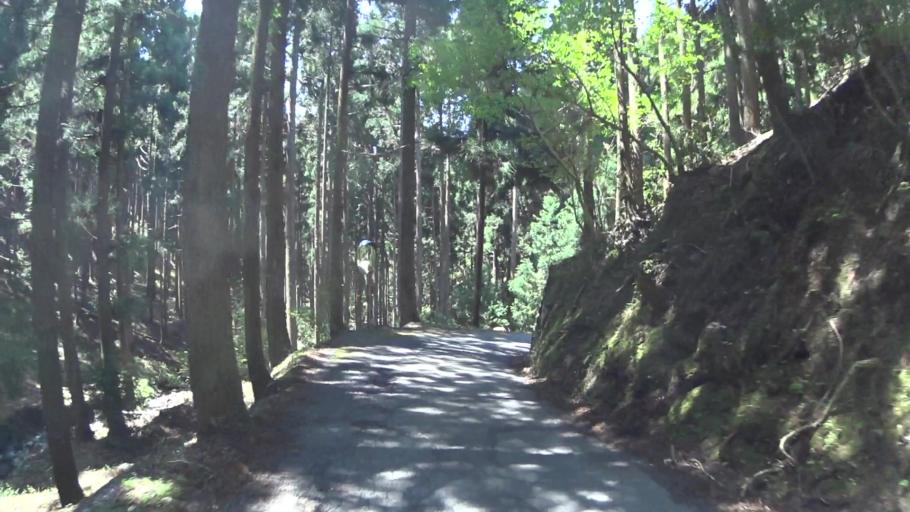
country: JP
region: Kyoto
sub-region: Kyoto-shi
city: Kamigyo-ku
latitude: 35.1498
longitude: 135.7872
